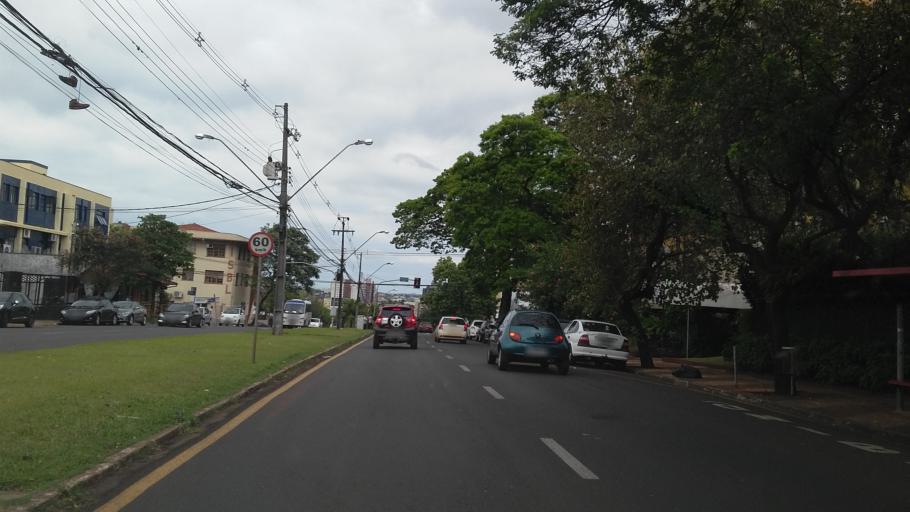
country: BR
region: Parana
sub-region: Londrina
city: Londrina
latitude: -23.3199
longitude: -51.1568
